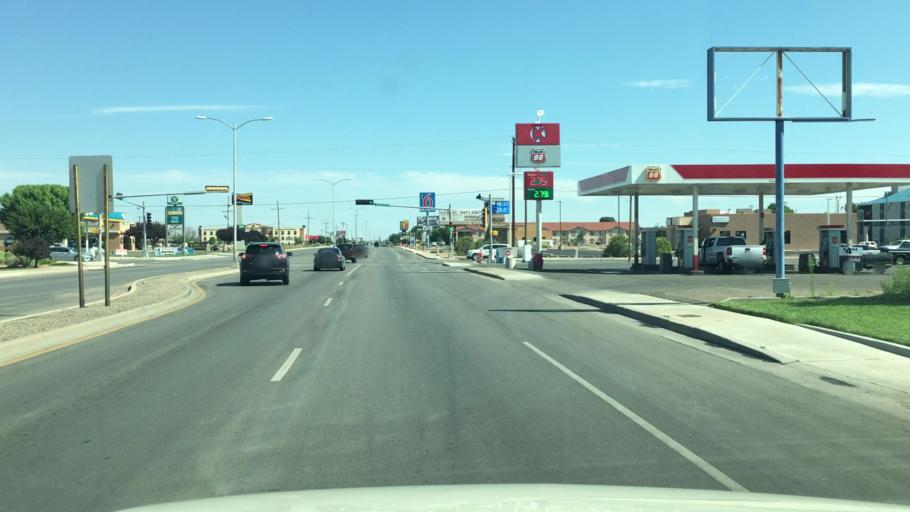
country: US
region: New Mexico
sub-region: Chaves County
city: Roswell
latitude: 33.4371
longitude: -104.5231
